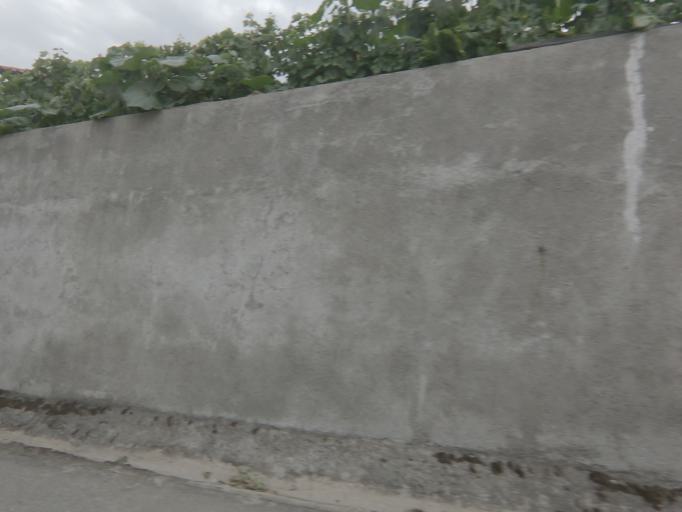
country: PT
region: Viseu
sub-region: Armamar
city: Armamar
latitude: 41.1255
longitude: -7.6609
